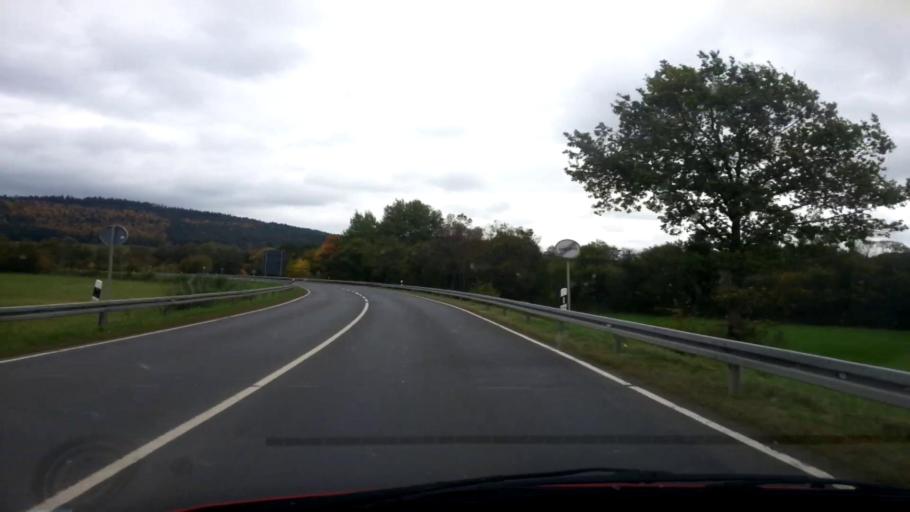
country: DE
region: Bavaria
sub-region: Upper Franconia
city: Kirchenpingarten
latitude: 49.9406
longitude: 11.7415
